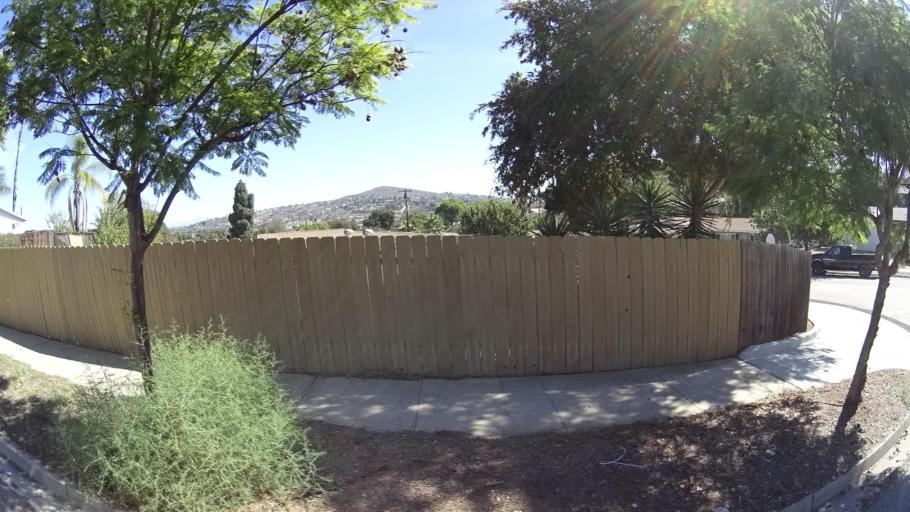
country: US
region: California
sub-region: San Diego County
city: Lemon Grove
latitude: 32.7217
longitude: -117.0229
